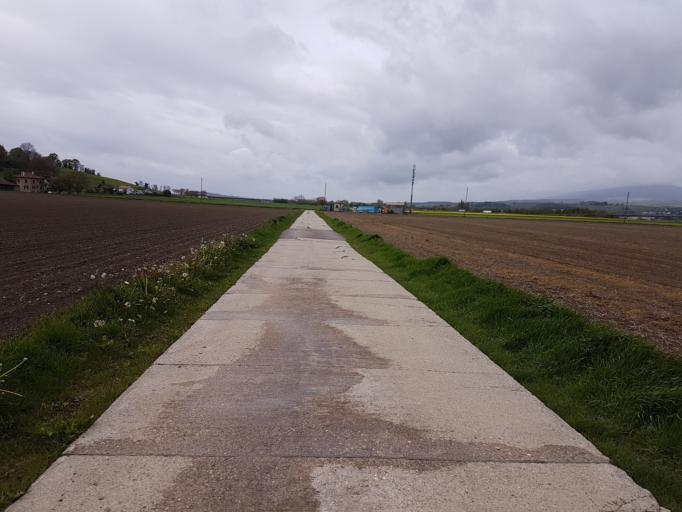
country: CH
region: Vaud
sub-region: Jura-Nord vaudois District
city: Chavornay
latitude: 46.7305
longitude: 6.5806
